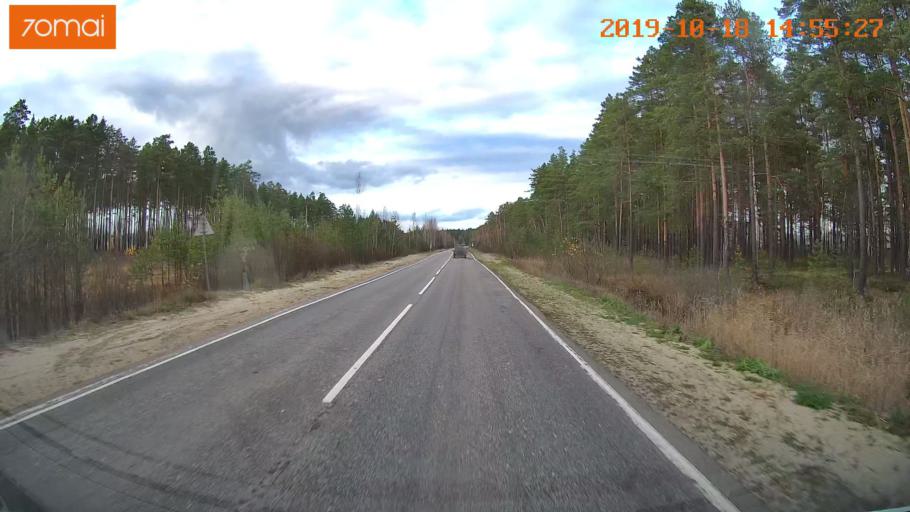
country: RU
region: Vladimir
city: Kurlovo
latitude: 55.4524
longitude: 40.5889
